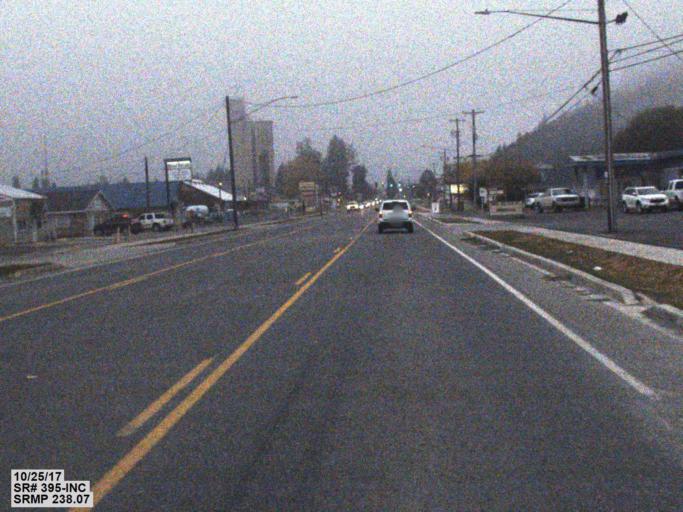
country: US
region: Washington
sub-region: Stevens County
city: Kettle Falls
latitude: 48.6110
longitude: -118.0532
